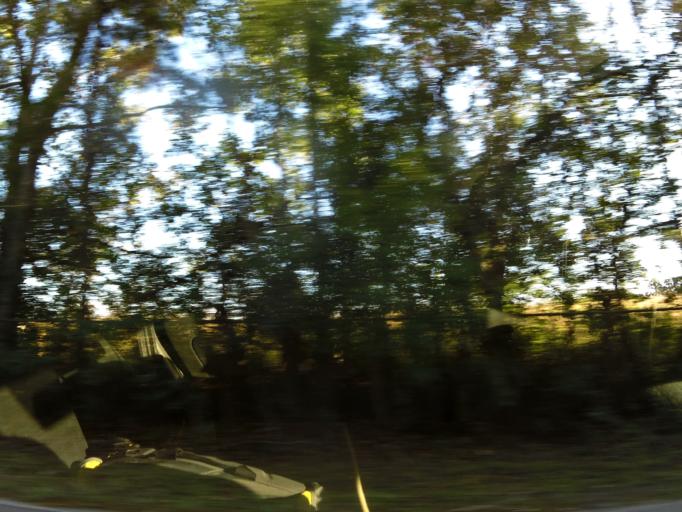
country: US
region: Florida
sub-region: Duval County
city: Jacksonville
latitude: 30.3689
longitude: -81.7415
